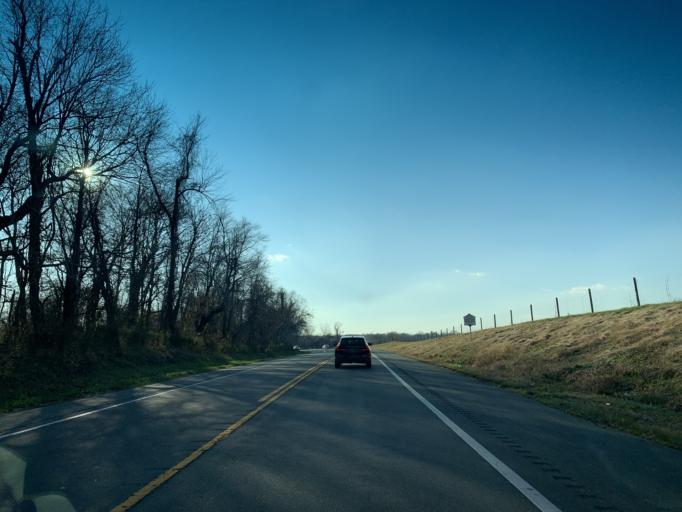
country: US
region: Maryland
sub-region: Cecil County
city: Elkton
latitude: 39.4663
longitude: -75.8649
